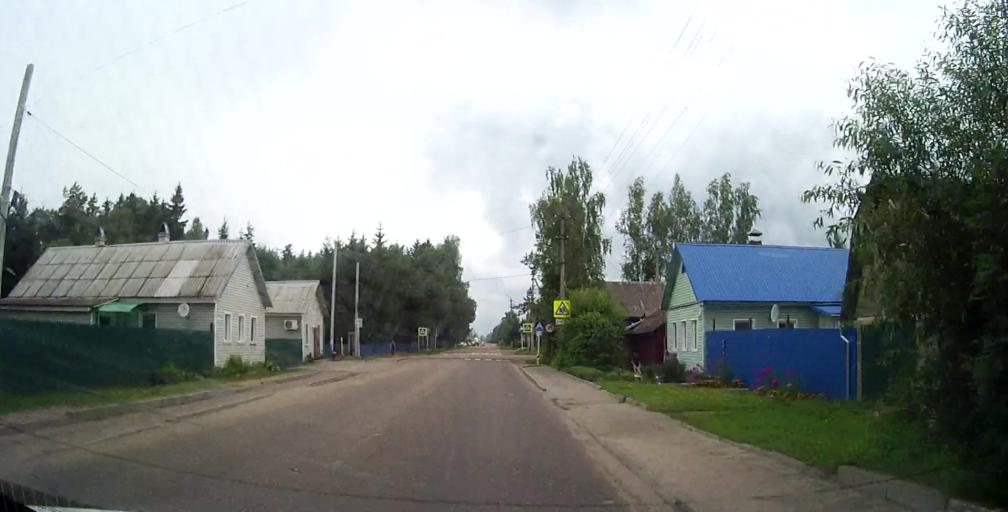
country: RU
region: Smolensk
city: Demidov
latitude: 55.2678
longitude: 31.5170
